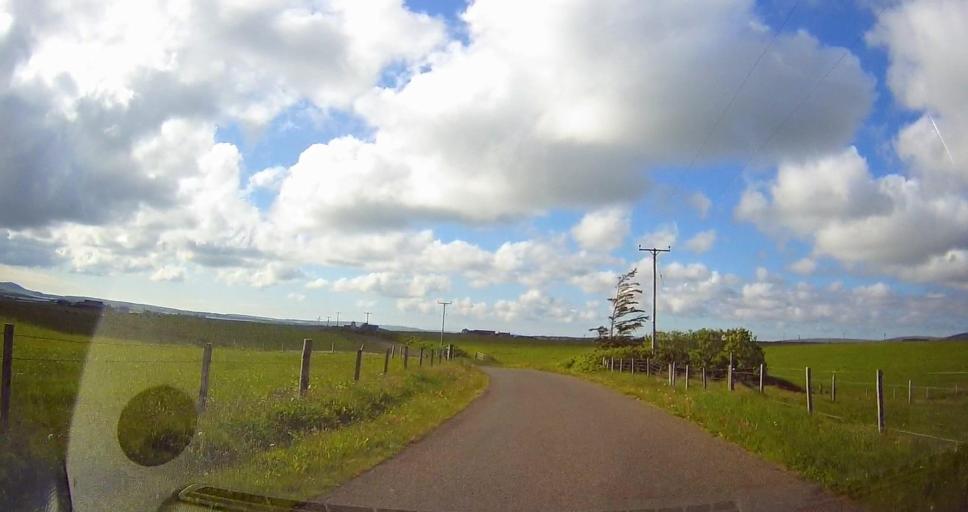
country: GB
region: Scotland
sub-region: Orkney Islands
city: Stromness
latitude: 58.9942
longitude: -3.1588
